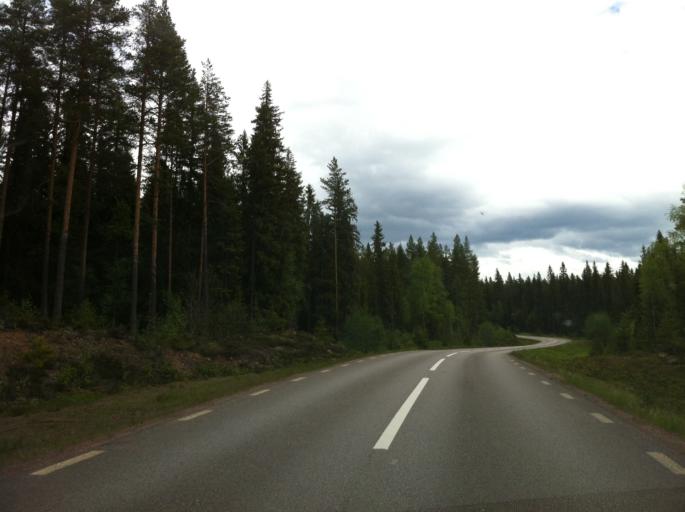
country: NO
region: Hedmark
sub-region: Trysil
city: Innbygda
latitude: 61.3059
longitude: 13.0758
